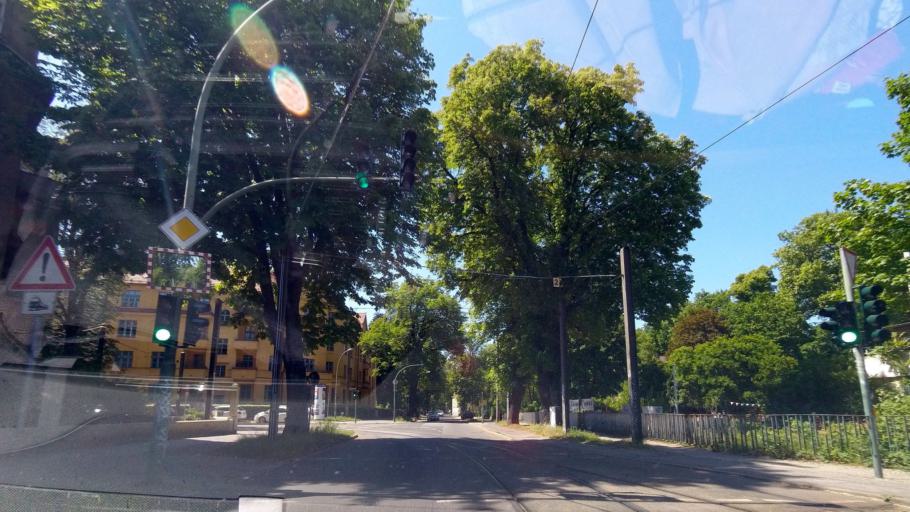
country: DE
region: Brandenburg
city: Potsdam
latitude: 52.3935
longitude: 13.0283
